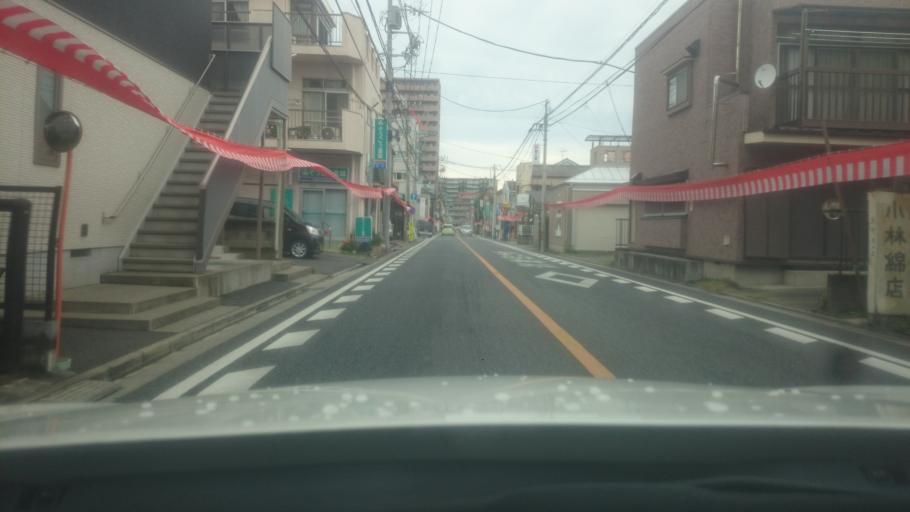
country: JP
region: Saitama
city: Kawagoe
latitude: 35.9135
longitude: 139.4856
